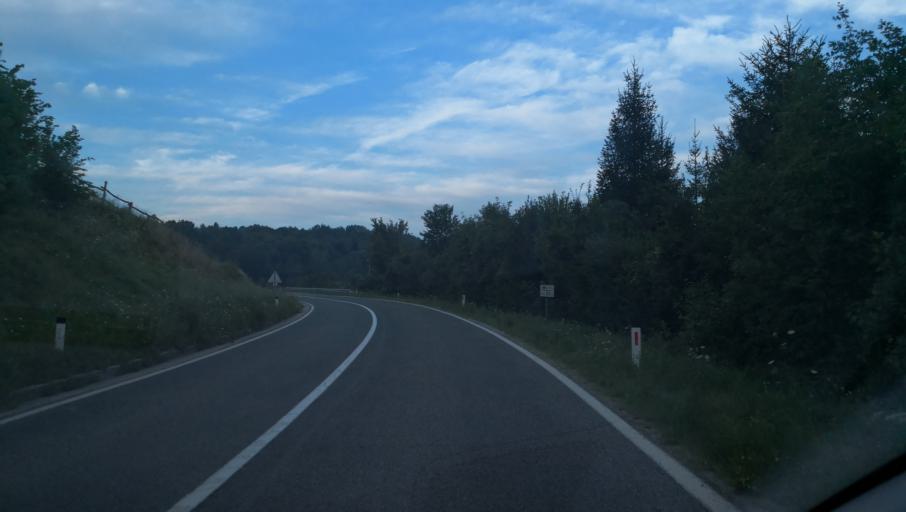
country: SI
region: Metlika
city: Metlika
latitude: 45.6634
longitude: 15.2896
